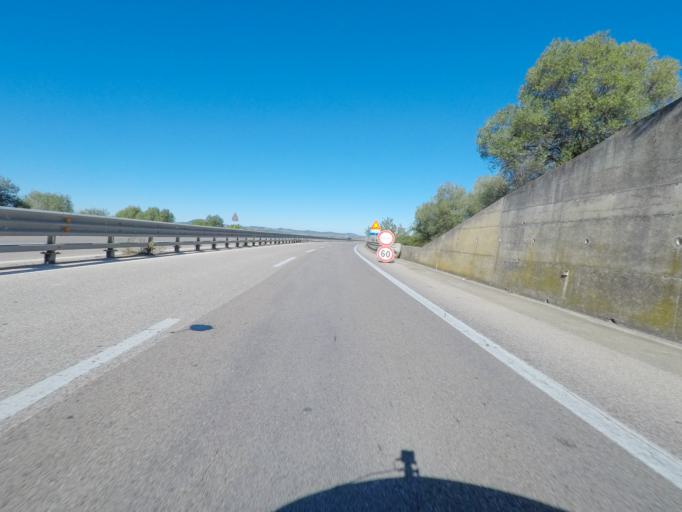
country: IT
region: Tuscany
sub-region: Provincia di Grosseto
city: Grosseto
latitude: 42.7385
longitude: 11.1382
